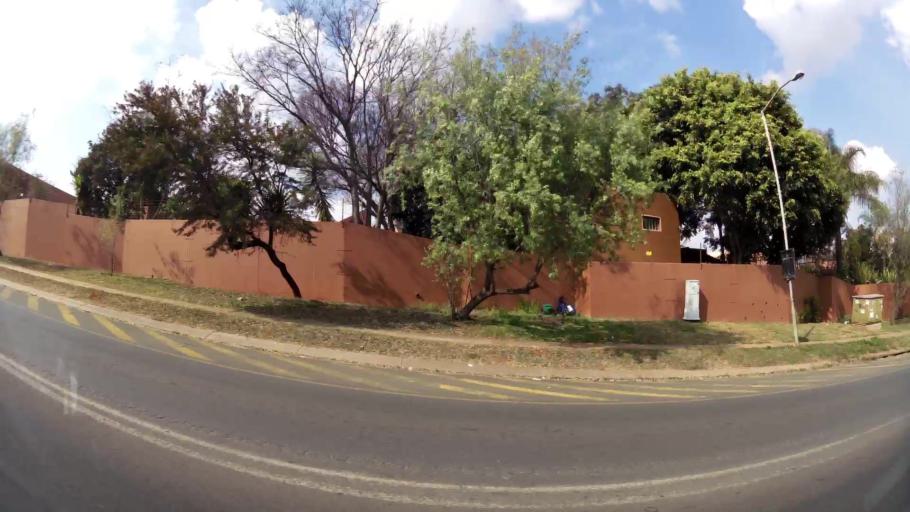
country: ZA
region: Gauteng
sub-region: City of Tshwane Metropolitan Municipality
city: Pretoria
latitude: -25.7854
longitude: 28.3158
